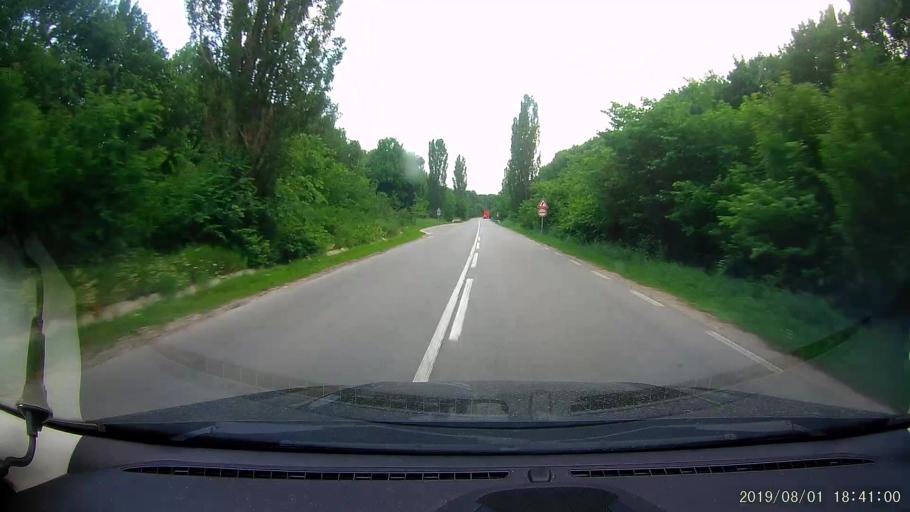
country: BG
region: Shumen
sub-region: Obshtina Khitrino
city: Gara Khitrino
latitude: 43.3540
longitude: 26.9225
